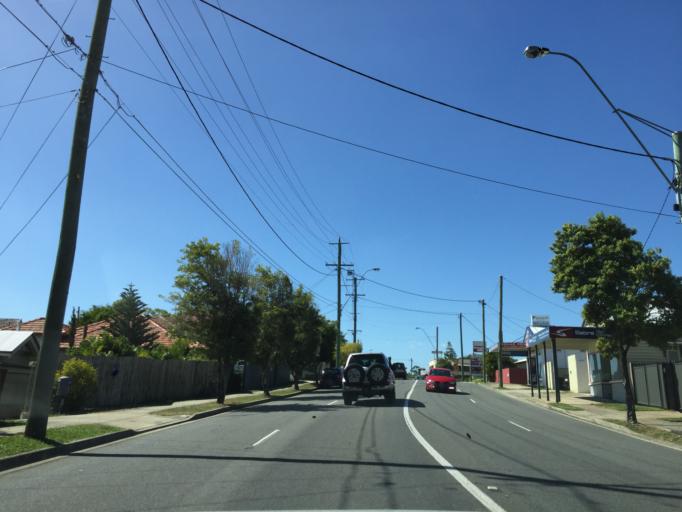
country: AU
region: Queensland
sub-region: Brisbane
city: Milton
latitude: -27.4464
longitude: 152.9855
